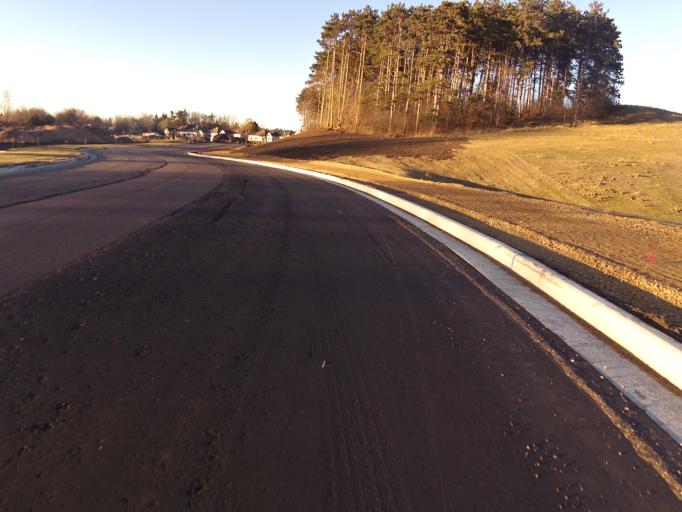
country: US
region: Wisconsin
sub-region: Saint Croix County
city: Hudson
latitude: 44.9650
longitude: -92.7282
